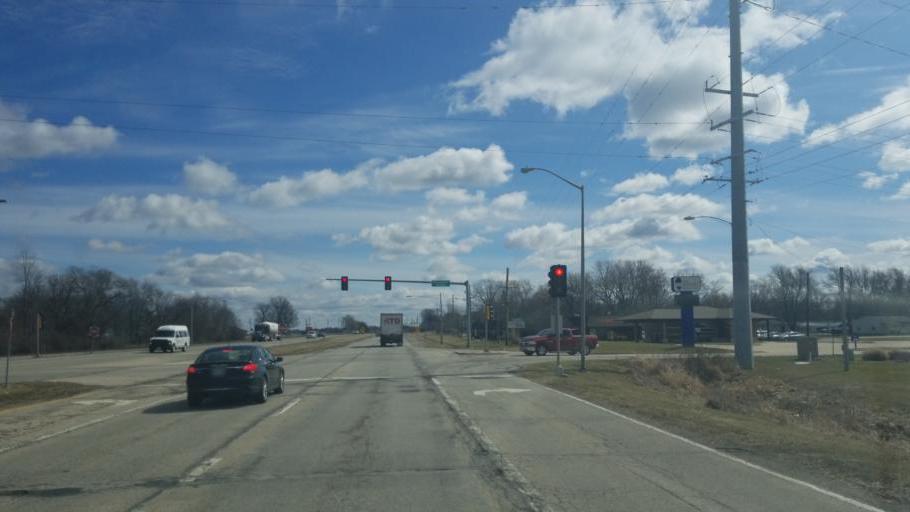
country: US
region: Illinois
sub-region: Macon County
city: Long Creek
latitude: 39.8243
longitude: -88.8930
